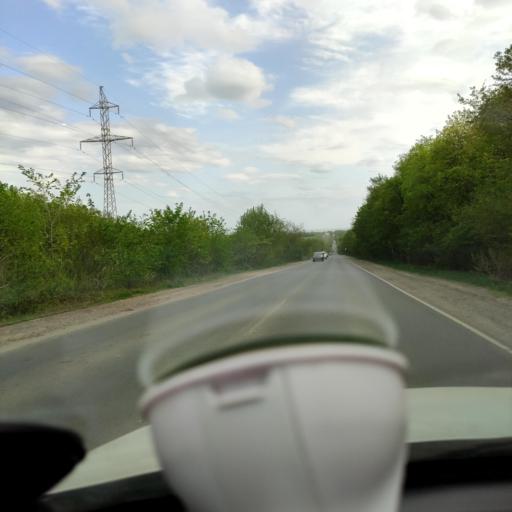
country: RU
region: Samara
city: Novosemeykino
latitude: 53.3290
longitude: 50.2586
